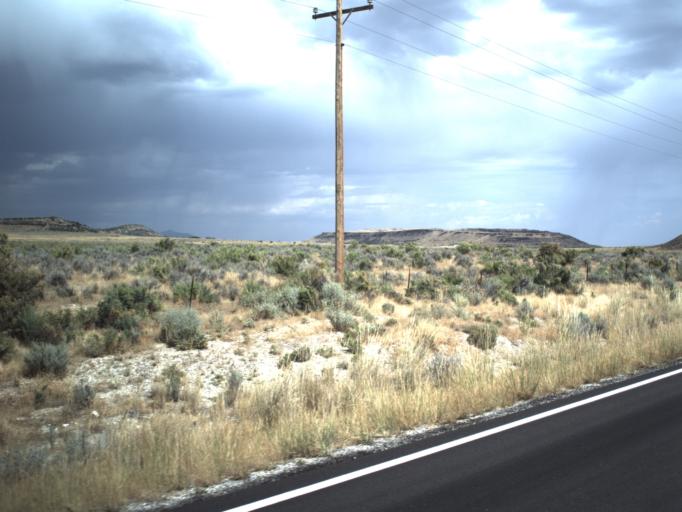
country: US
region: Idaho
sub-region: Minidoka County
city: Heyburn
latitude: 41.8215
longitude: -113.1908
